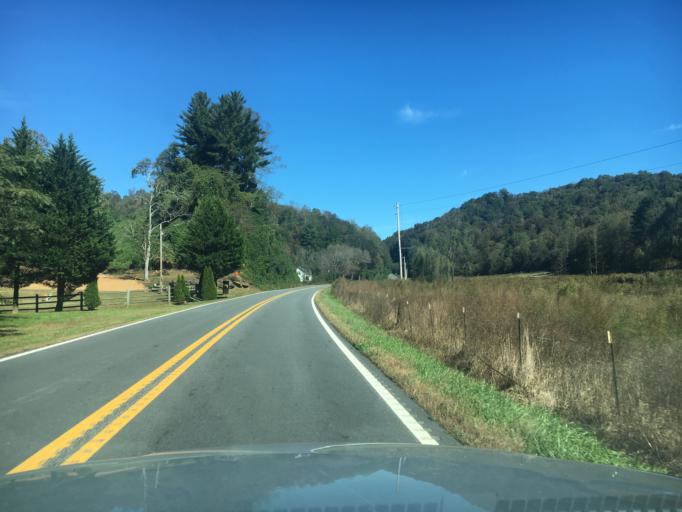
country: US
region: North Carolina
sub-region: Burke County
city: Glen Alpine
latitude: 35.5563
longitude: -81.8546
